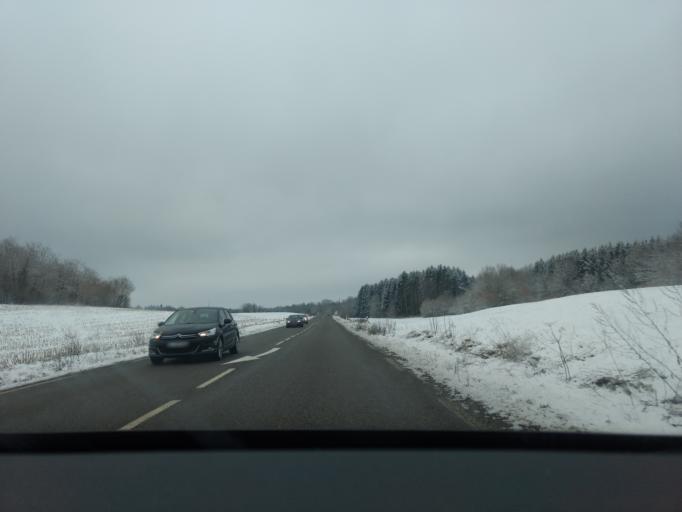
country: FR
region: Franche-Comte
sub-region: Departement du Jura
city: Champagnole
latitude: 46.7872
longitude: 5.8513
